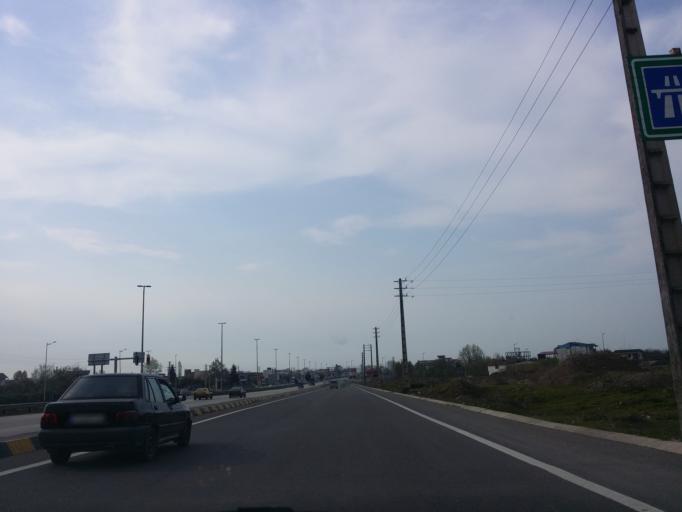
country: IR
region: Mazandaran
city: Chalus
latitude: 36.6544
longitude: 51.4040
